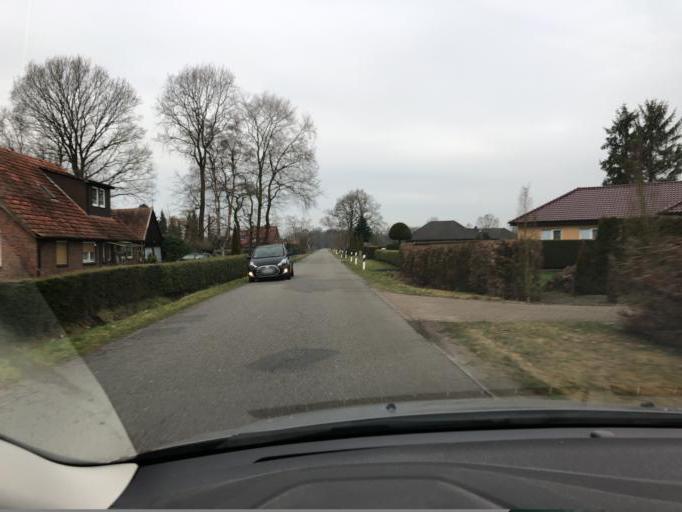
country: DE
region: Lower Saxony
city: Bad Zwischenahn
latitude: 53.1678
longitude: 8.0343
